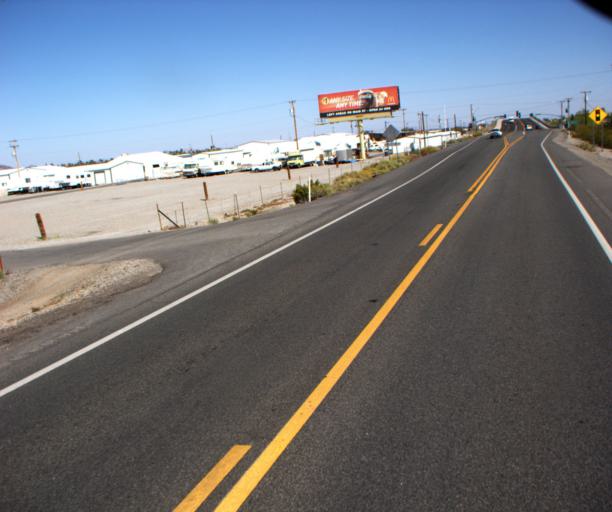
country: US
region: Arizona
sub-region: La Paz County
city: Quartzsite
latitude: 33.6581
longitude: -114.2171
